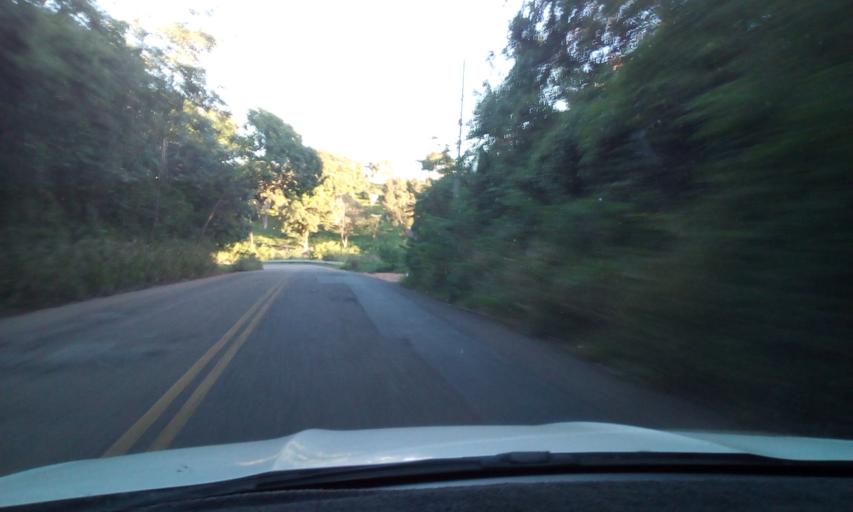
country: BR
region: Paraiba
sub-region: Areia
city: Areia
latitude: -6.9775
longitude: -35.7270
